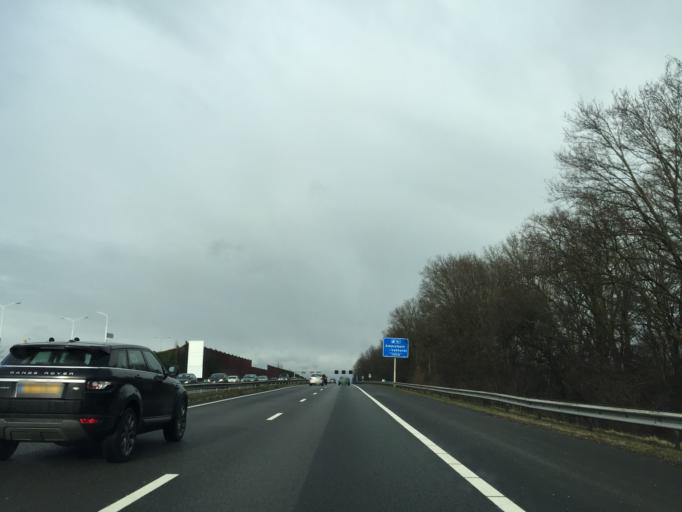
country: NL
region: Gelderland
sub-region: Gemeente Nijkerk
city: Nijkerk
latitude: 52.1938
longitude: 5.4396
